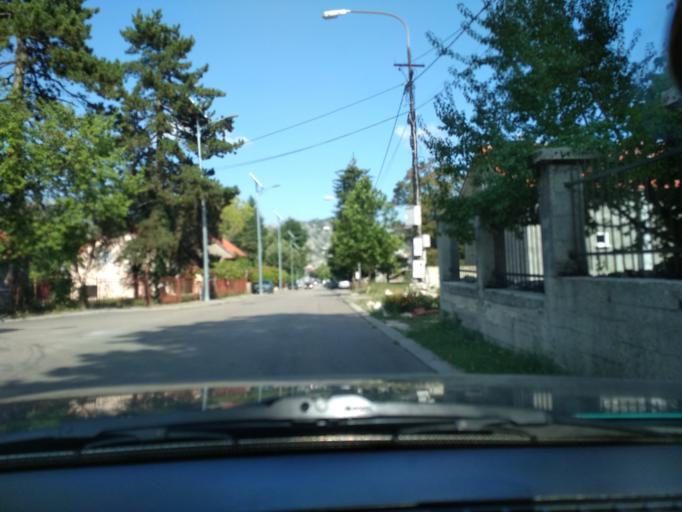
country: ME
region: Cetinje
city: Cetinje
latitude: 42.3925
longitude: 18.9083
